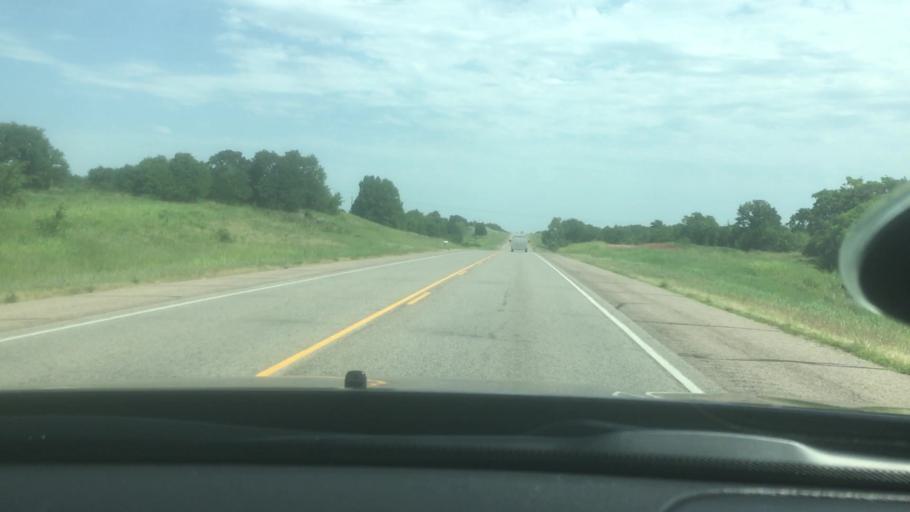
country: US
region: Oklahoma
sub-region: Seminole County
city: Konawa
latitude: 35.0208
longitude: -96.9314
